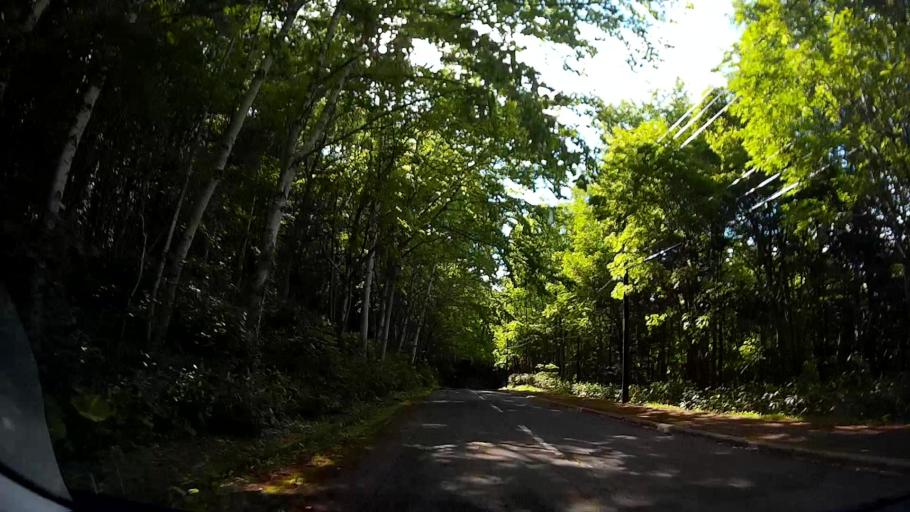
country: JP
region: Hokkaido
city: Sapporo
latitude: 42.9308
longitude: 141.1590
